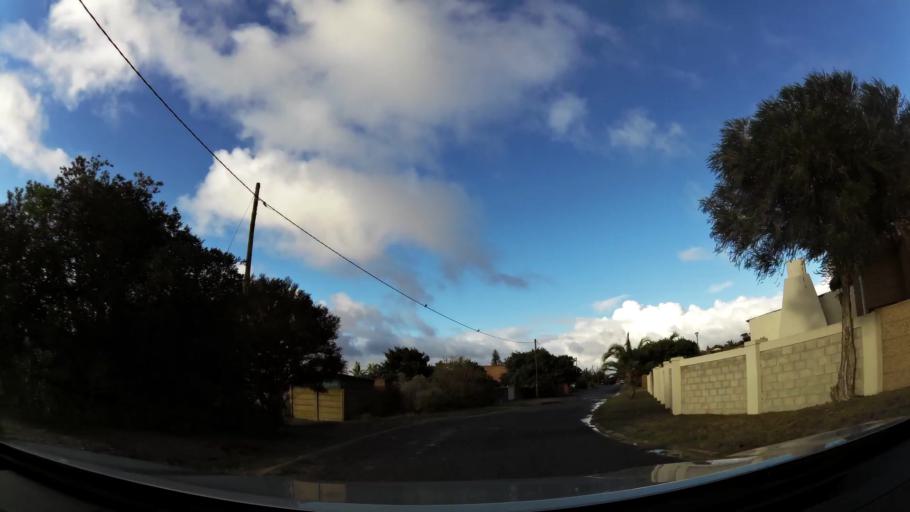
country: ZA
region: Western Cape
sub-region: Eden District Municipality
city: Riversdale
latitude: -34.2085
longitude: 21.5807
